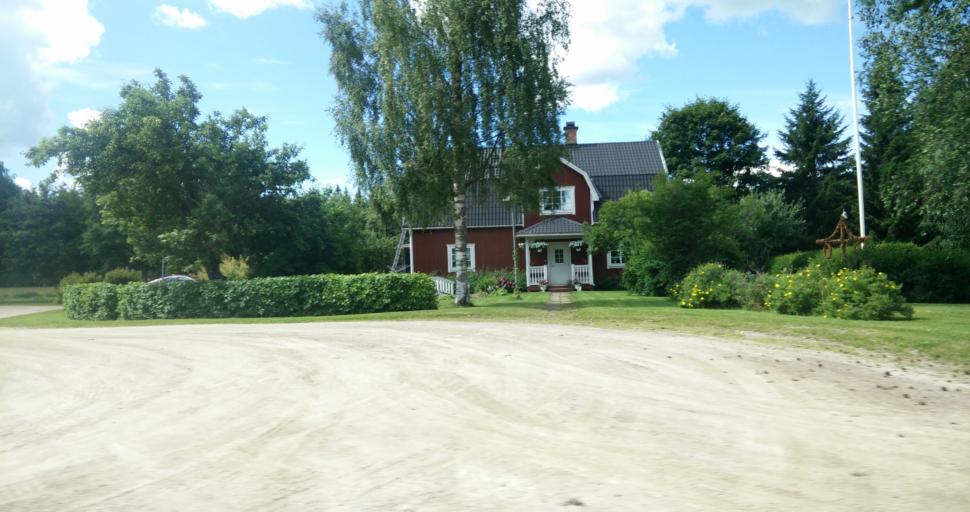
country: SE
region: Vaermland
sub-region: Hagfors Kommun
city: Ekshaerad
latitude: 60.0472
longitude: 13.4908
